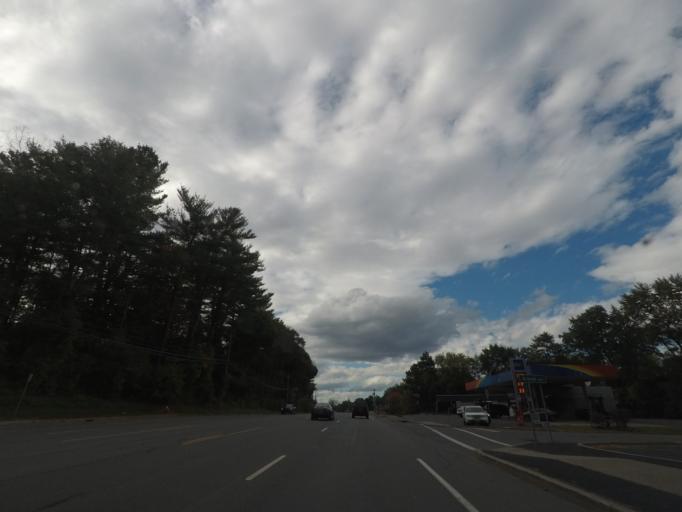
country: US
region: New York
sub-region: Albany County
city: Westmere
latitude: 42.6954
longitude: -73.8809
